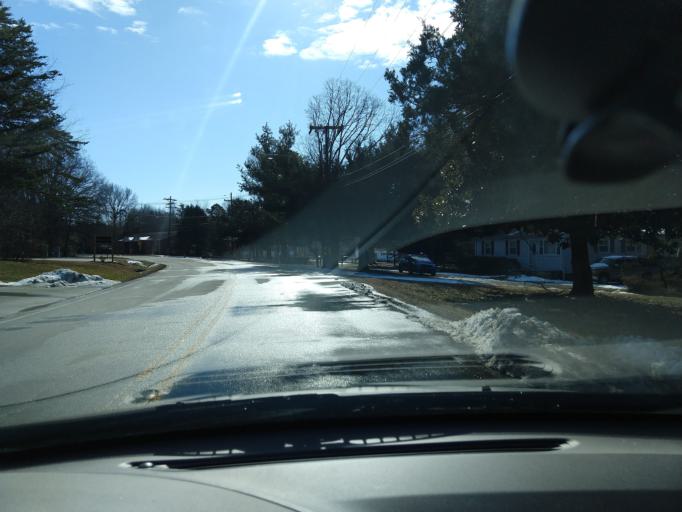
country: US
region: North Carolina
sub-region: Guilford County
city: Greensboro
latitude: 36.1274
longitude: -79.8459
